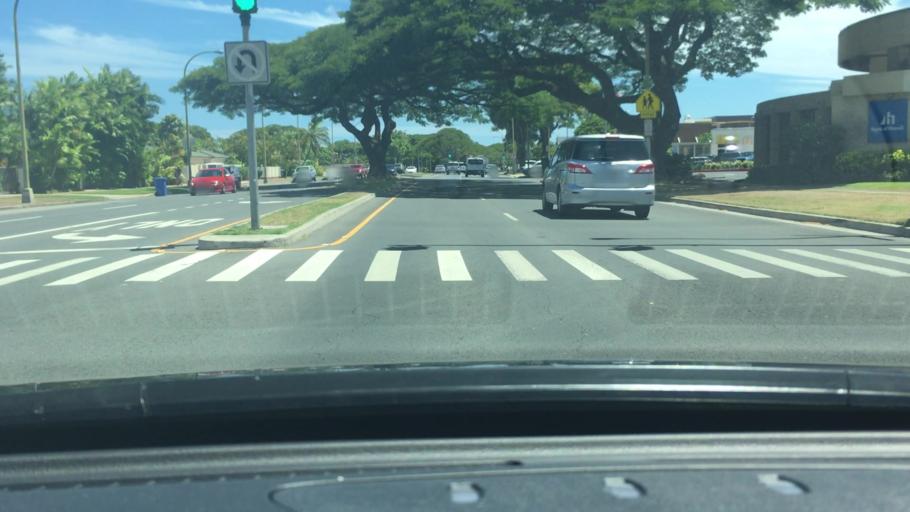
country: US
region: Hawaii
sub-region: Honolulu County
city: Honolulu
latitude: 21.2763
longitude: -157.7849
